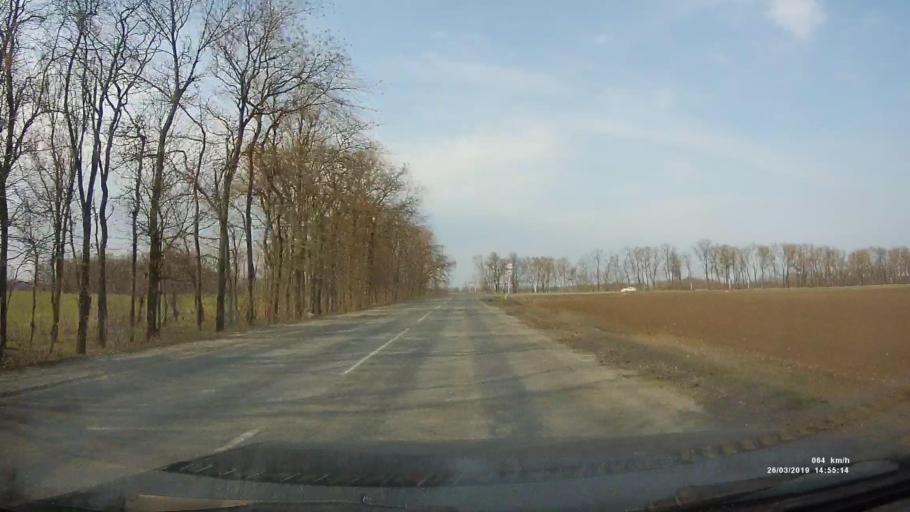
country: RU
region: Rostov
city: Novobessergenovka
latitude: 47.2024
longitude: 38.8104
